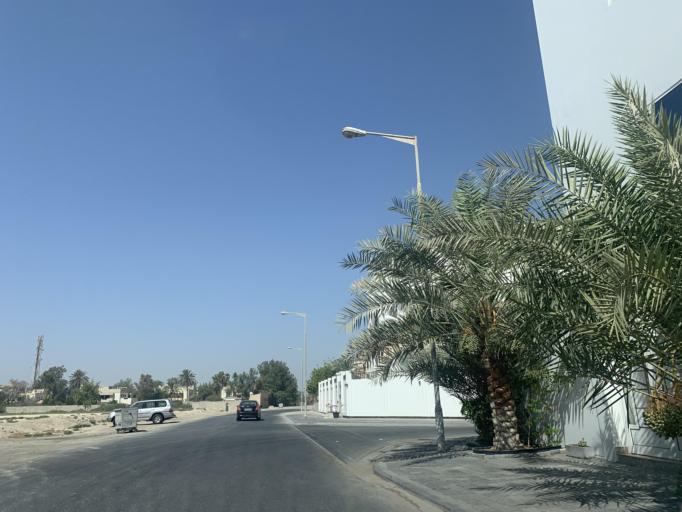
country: BH
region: Manama
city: Jidd Hafs
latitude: 26.2240
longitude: 50.5293
